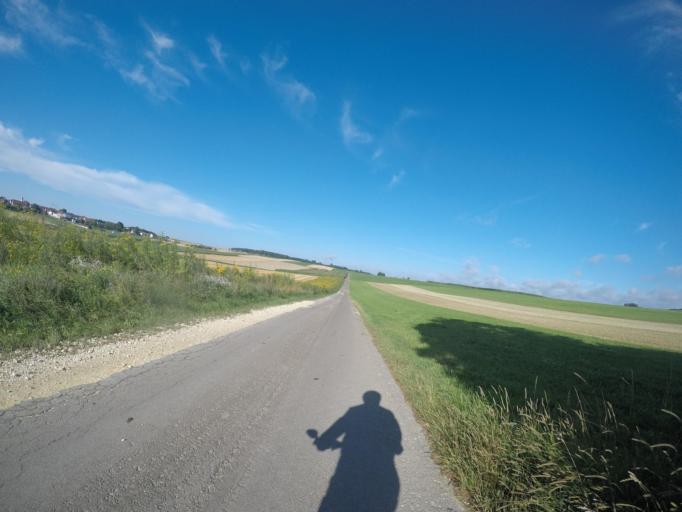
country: DE
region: Baden-Wuerttemberg
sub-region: Tuebingen Region
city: Schelklingen
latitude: 48.3952
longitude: 9.7182
